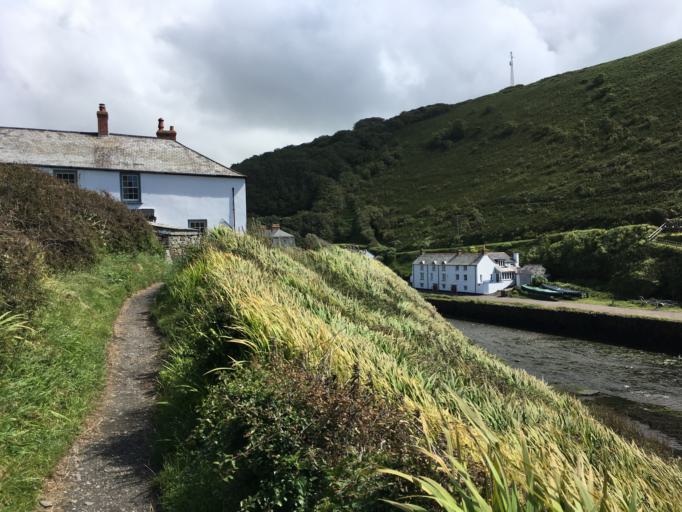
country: GB
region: England
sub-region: Cornwall
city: Tintagel
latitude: 50.6917
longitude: -4.6969
